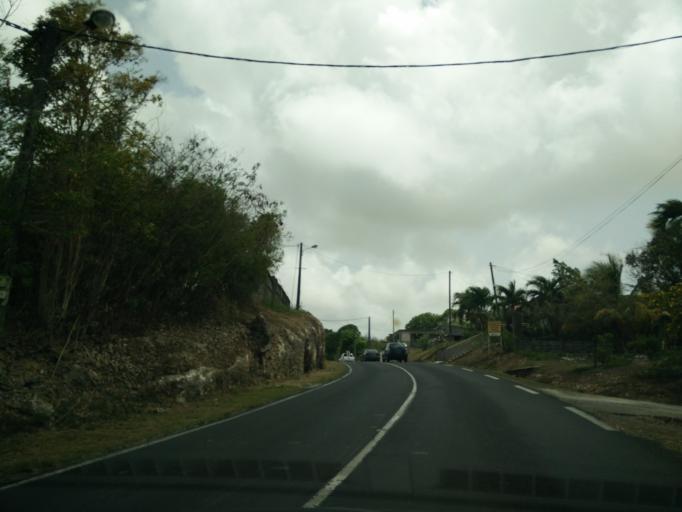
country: GP
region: Guadeloupe
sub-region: Guadeloupe
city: Petit-Canal
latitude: 16.3621
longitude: -61.4561
